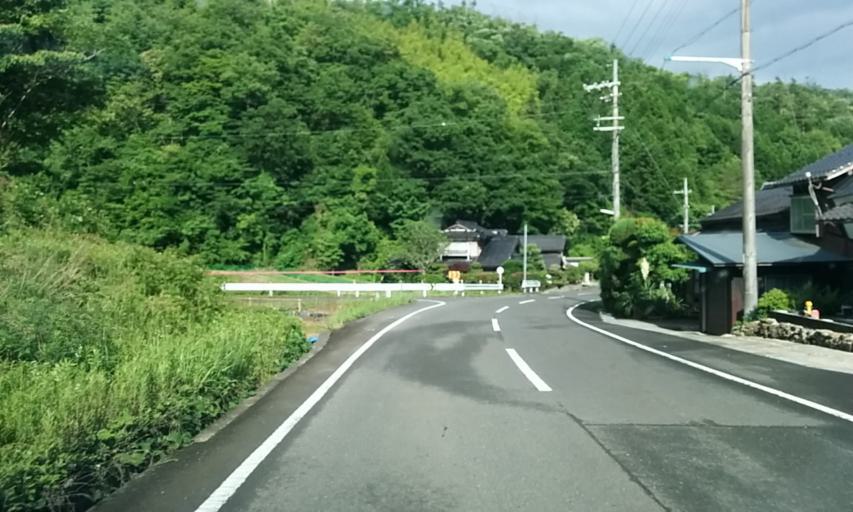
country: JP
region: Kyoto
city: Ayabe
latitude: 35.3712
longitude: 135.2866
